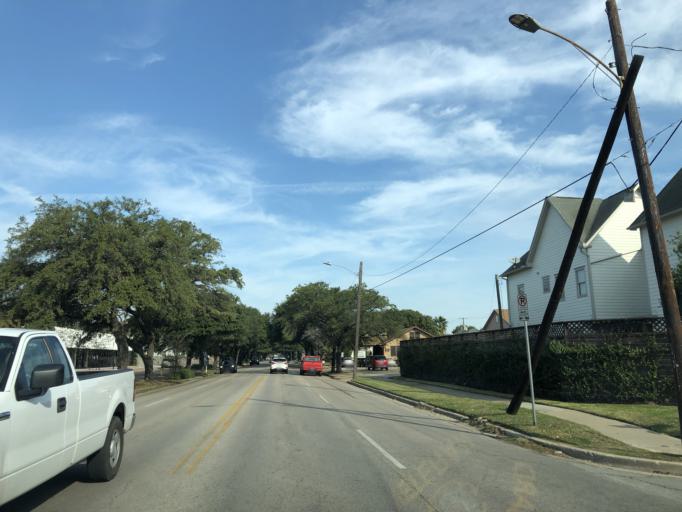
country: US
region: Texas
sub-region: Harris County
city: Houston
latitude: 29.7942
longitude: -95.3990
